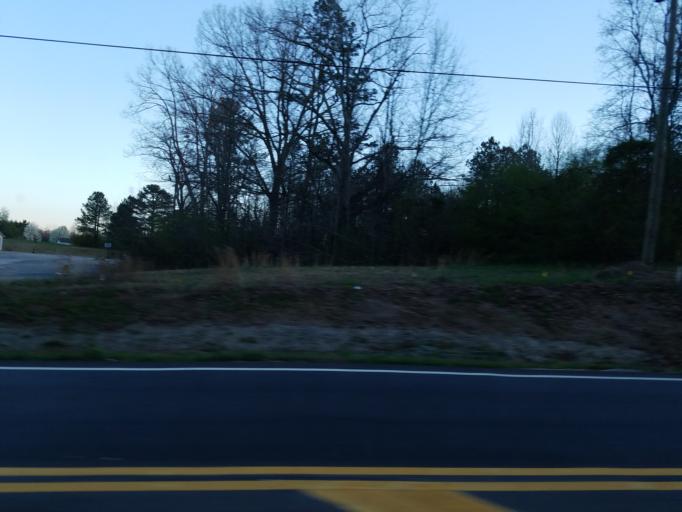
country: US
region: Georgia
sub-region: Forsyth County
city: Cumming
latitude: 34.2865
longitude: -84.0326
